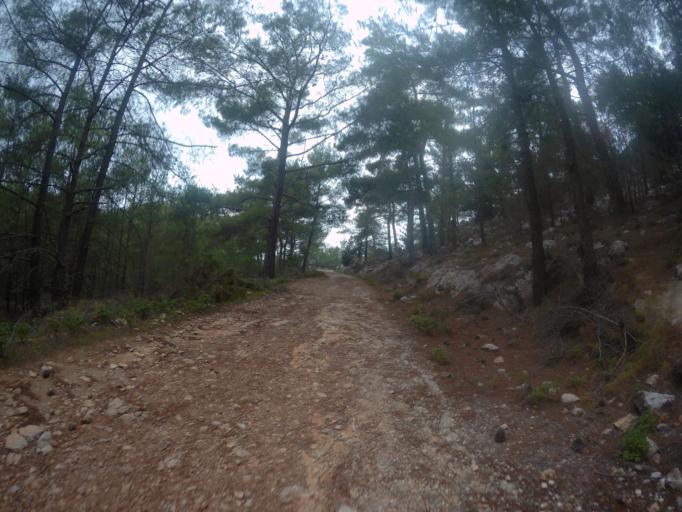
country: CY
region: Ammochostos
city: Lefkonoiko
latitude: 35.2941
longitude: 33.5519
